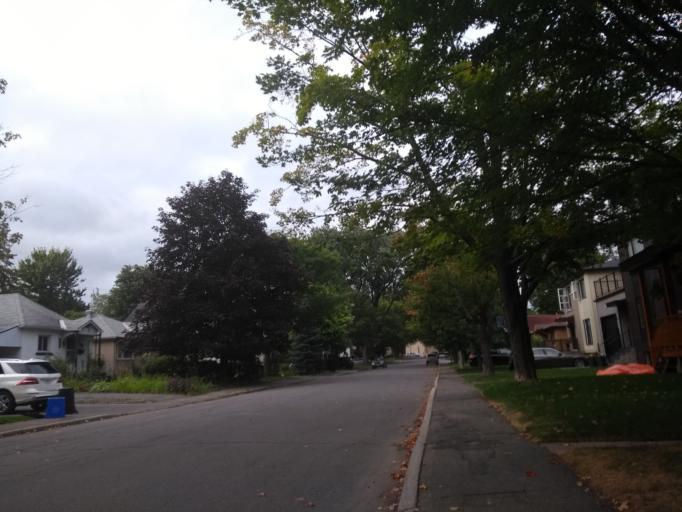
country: CA
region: Ontario
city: Ottawa
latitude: 45.4033
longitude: -75.6721
